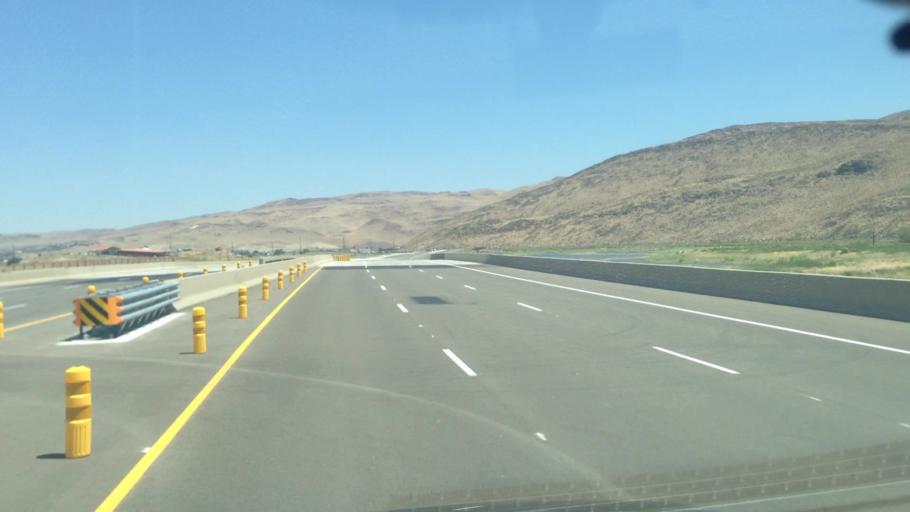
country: US
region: Nevada
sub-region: Washoe County
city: Sparks
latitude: 39.5042
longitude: -119.7242
